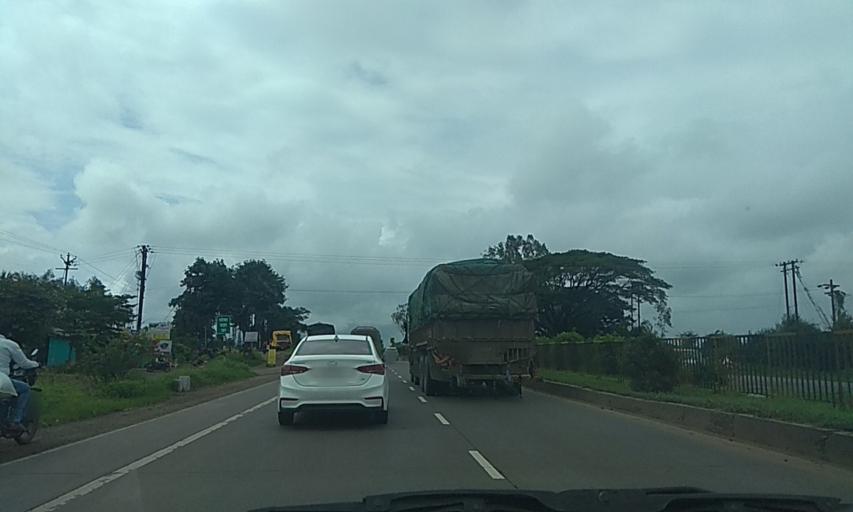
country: IN
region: Maharashtra
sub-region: Kolhapur
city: Kolhapur
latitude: 16.6470
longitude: 74.2751
